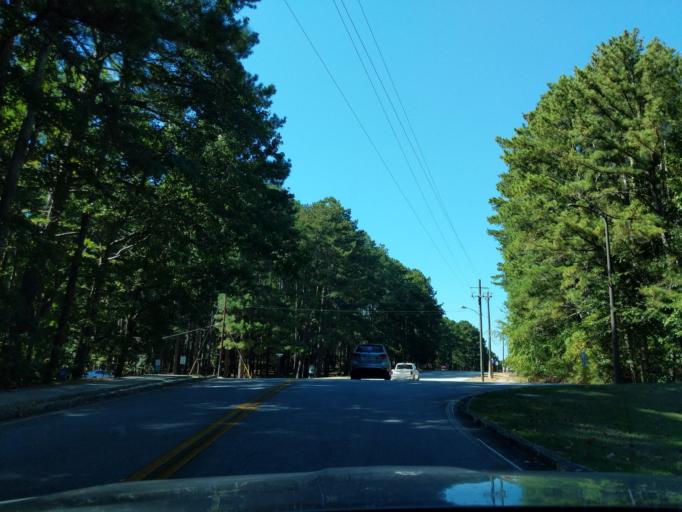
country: US
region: Georgia
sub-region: DeKalb County
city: Stone Mountain
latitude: 33.8083
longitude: -84.1366
